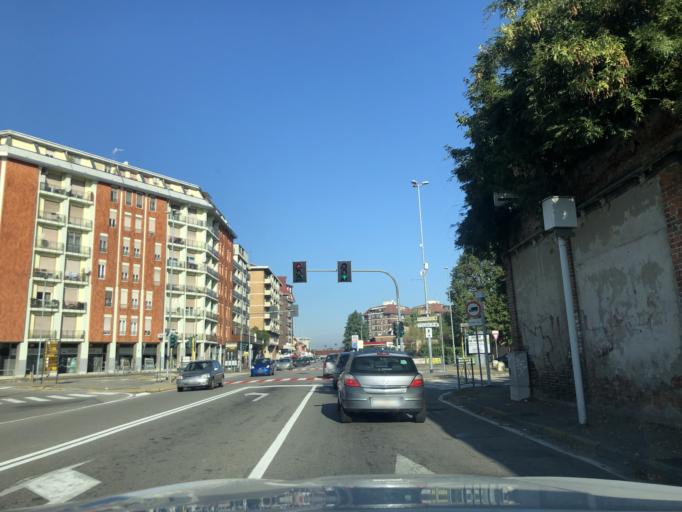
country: IT
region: Lombardy
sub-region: Citta metropolitana di Milano
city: Baranzate
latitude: 45.5264
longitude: 9.1127
